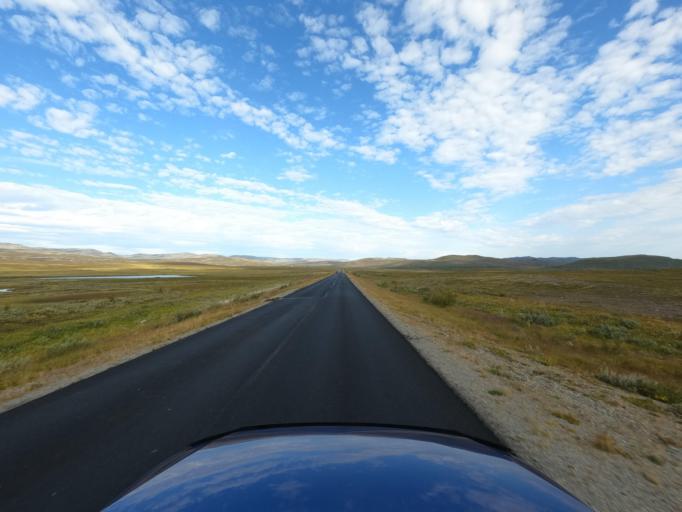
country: NO
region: Finnmark Fylke
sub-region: Kvalsund
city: Kvalsund
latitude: 70.2405
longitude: 24.0845
